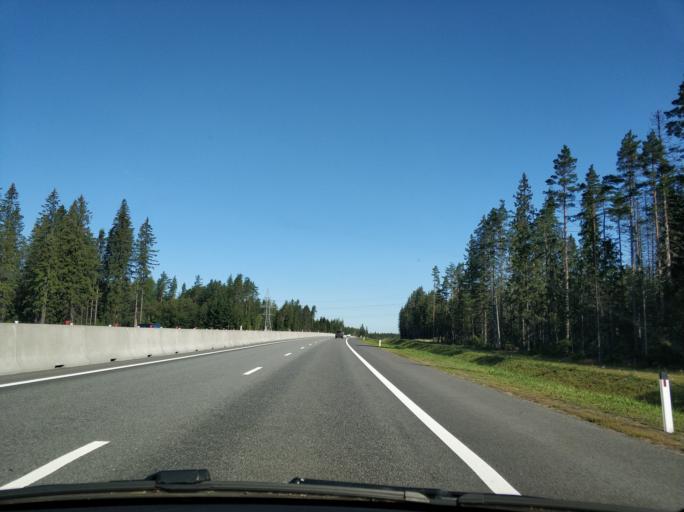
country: RU
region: Leningrad
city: Sosnovo
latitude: 60.5221
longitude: 30.1712
